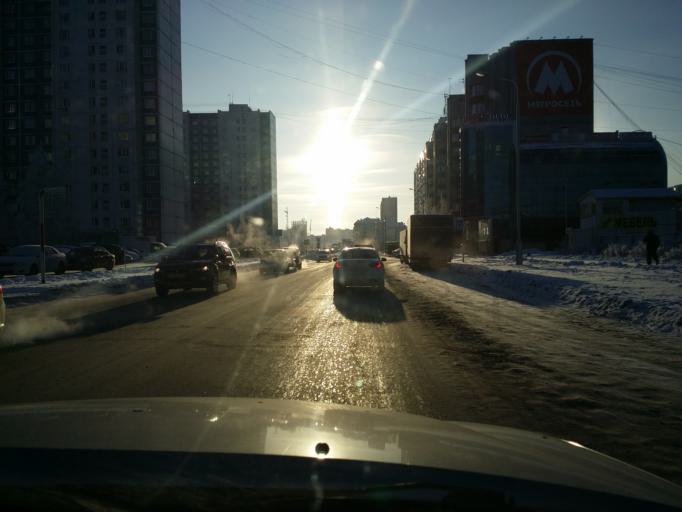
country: RU
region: Khanty-Mansiyskiy Avtonomnyy Okrug
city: Nizhnevartovsk
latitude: 60.9398
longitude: 76.5894
